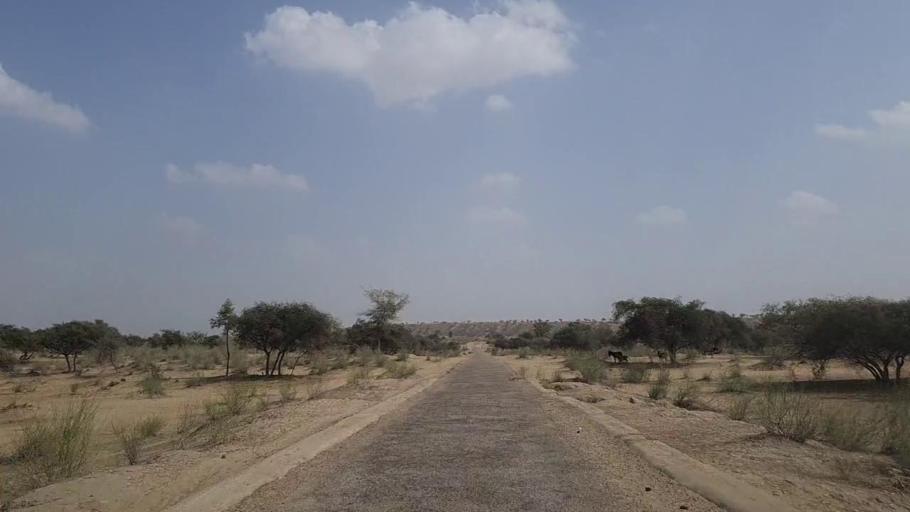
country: PK
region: Sindh
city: Islamkot
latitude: 24.7885
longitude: 70.0876
